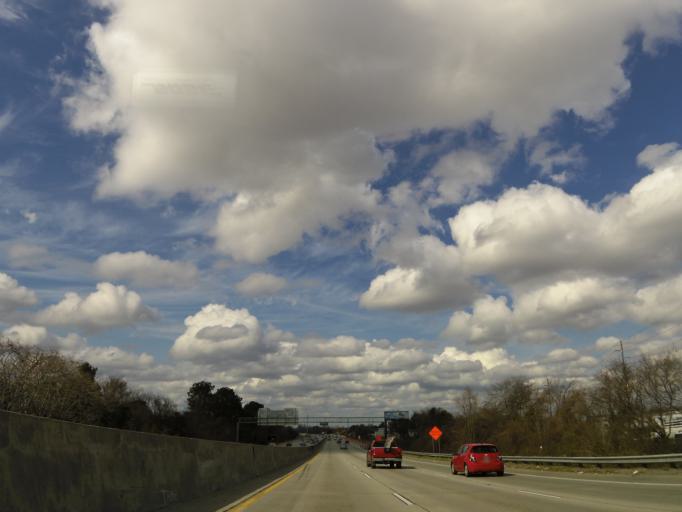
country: US
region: South Carolina
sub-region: Charleston County
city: North Charleston
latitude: 32.8275
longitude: -79.9542
